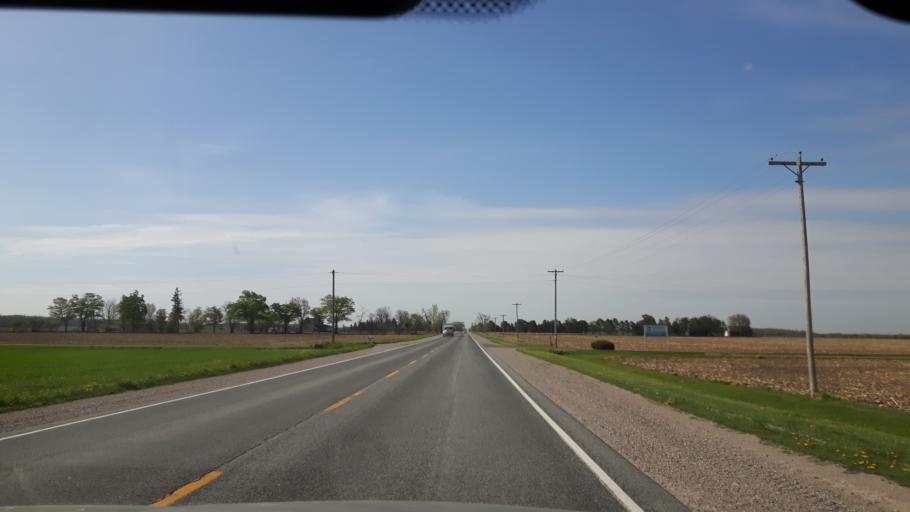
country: CA
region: Ontario
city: Bluewater
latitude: 43.4881
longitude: -81.5095
